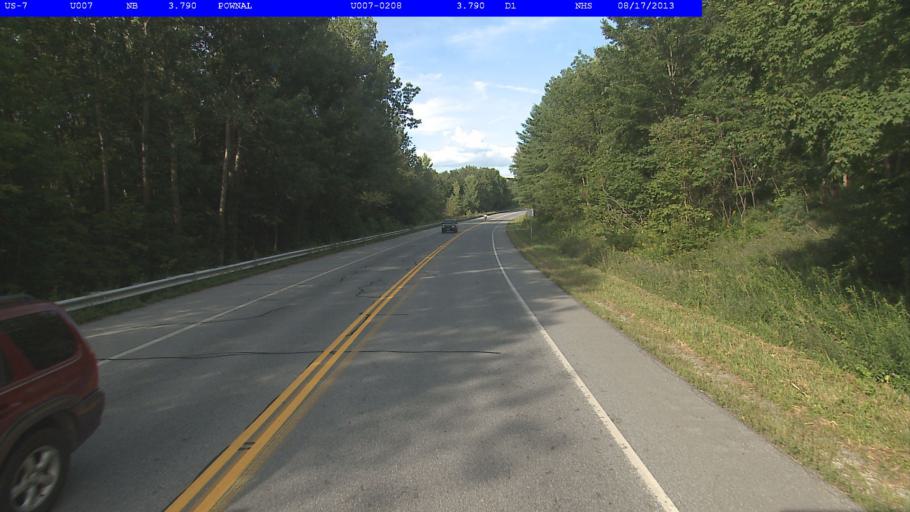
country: US
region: Massachusetts
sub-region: Berkshire County
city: Williamstown
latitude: 42.7888
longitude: -73.2389
